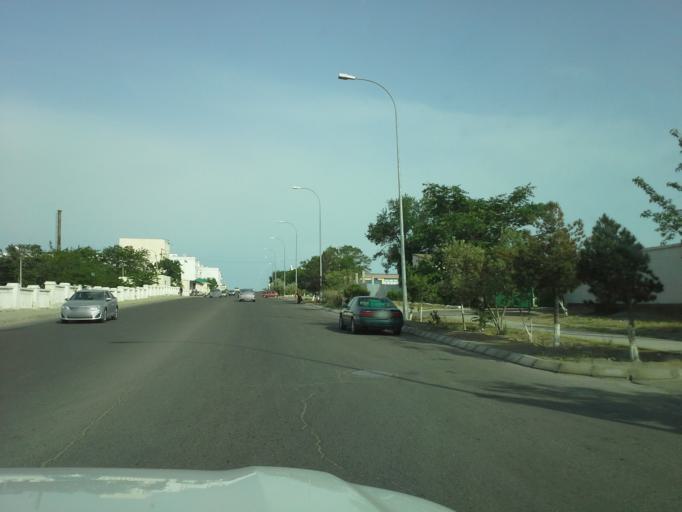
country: TM
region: Balkan
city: Turkmenbasy
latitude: 40.0192
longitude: 52.9715
